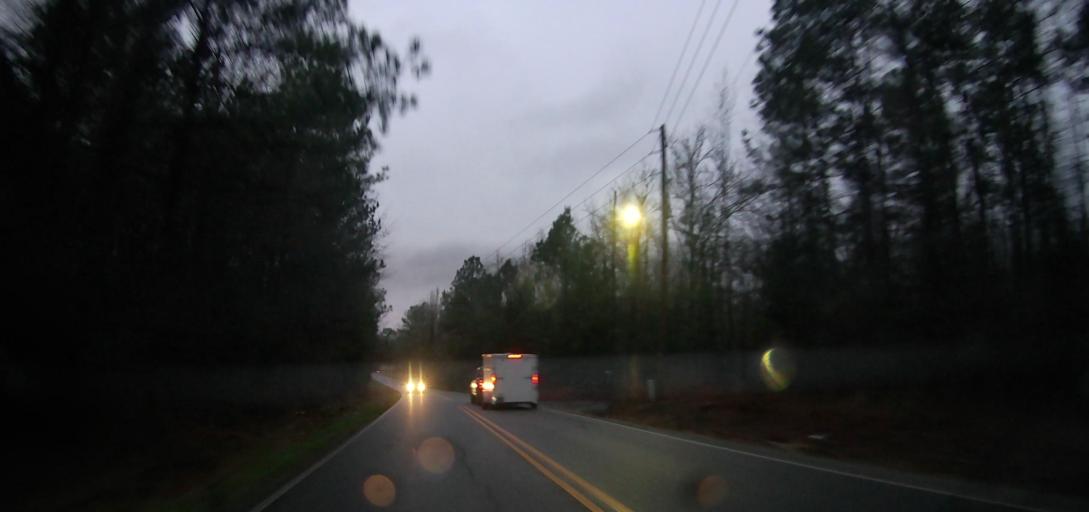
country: US
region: Alabama
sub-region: Tuscaloosa County
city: Vance
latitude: 33.1274
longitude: -87.2292
